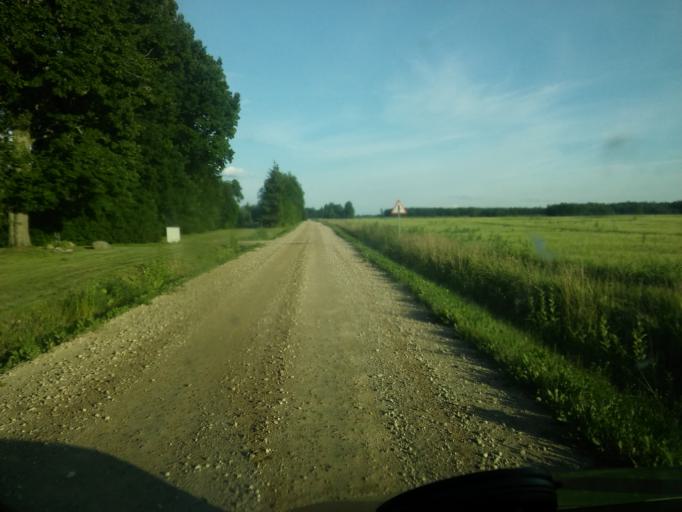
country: EE
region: Valgamaa
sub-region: Torva linn
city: Torva
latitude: 58.0668
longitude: 25.9062
